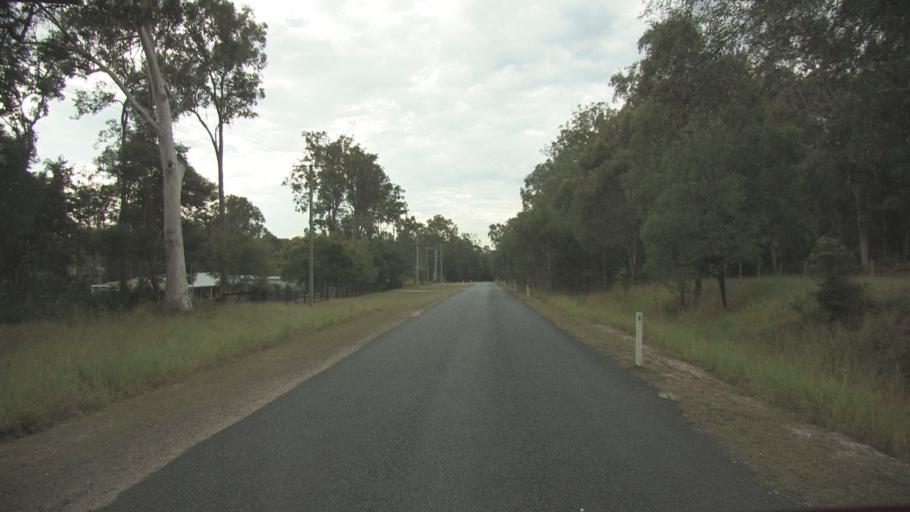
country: AU
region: Queensland
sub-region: Logan
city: Chambers Flat
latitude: -27.7857
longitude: 153.1089
